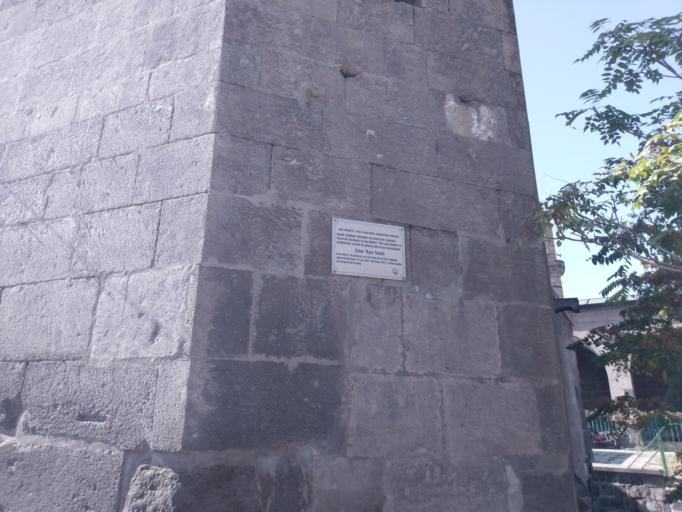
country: TR
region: Kayseri
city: Kayseri
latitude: 38.7172
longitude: 35.4932
